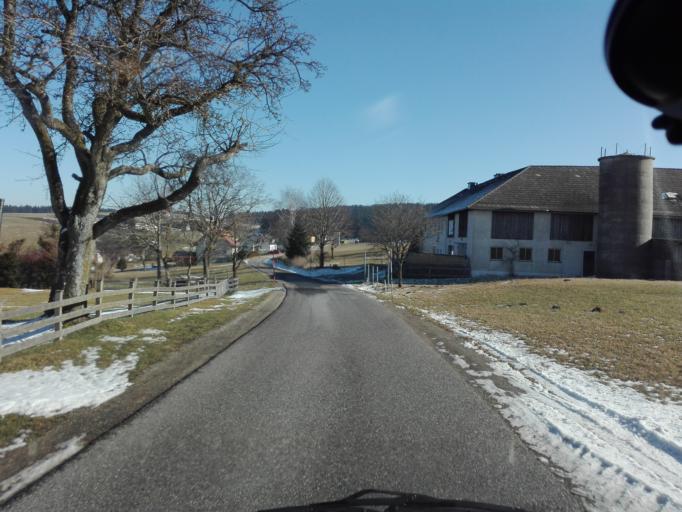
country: AT
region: Upper Austria
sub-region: Politischer Bezirk Urfahr-Umgebung
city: Sonnberg im Muehlkreis
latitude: 48.4590
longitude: 14.2951
